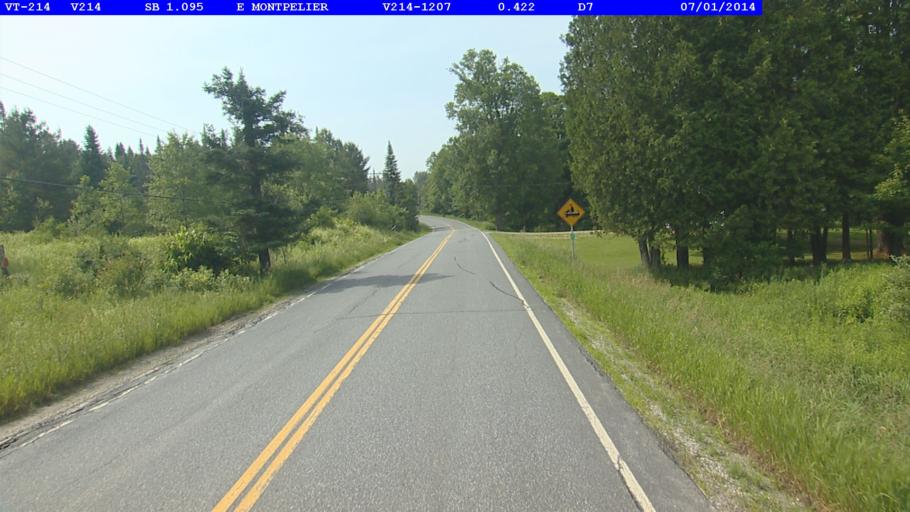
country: US
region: Vermont
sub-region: Washington County
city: Barre
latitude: 44.2913
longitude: -72.4446
